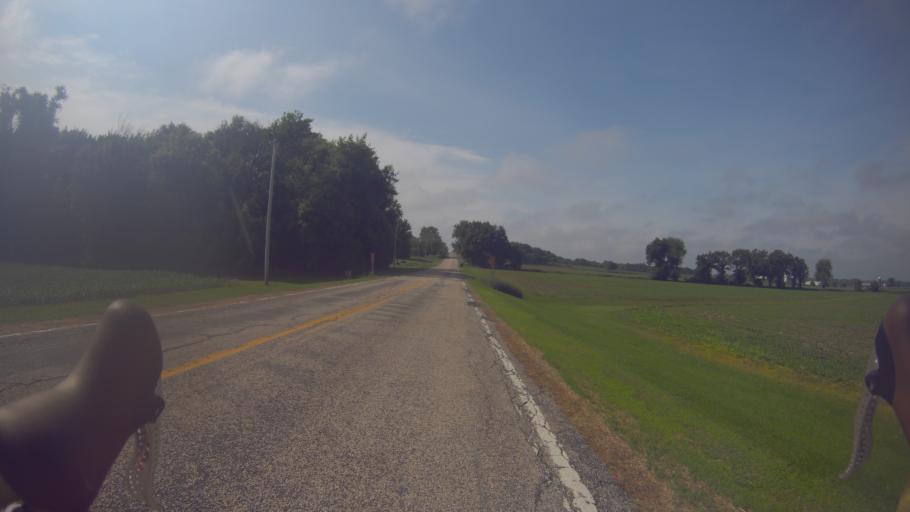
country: US
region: Wisconsin
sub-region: Dane County
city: Stoughton
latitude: 42.9680
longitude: -89.1808
